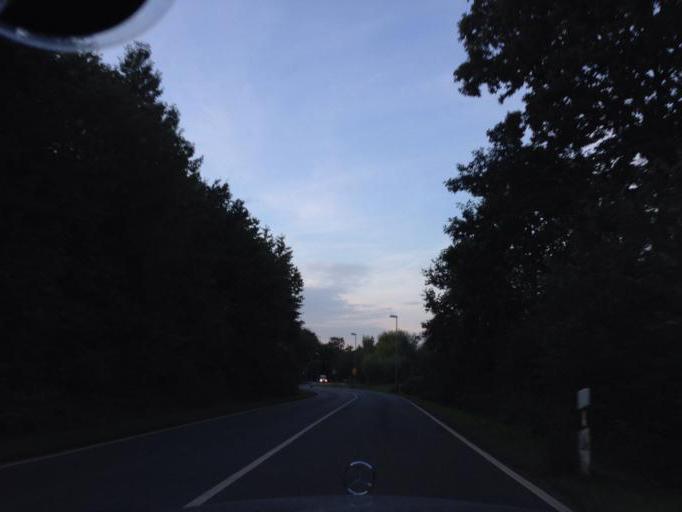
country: DE
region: Schleswig-Holstein
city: Bargteheide
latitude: 53.7213
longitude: 10.2650
